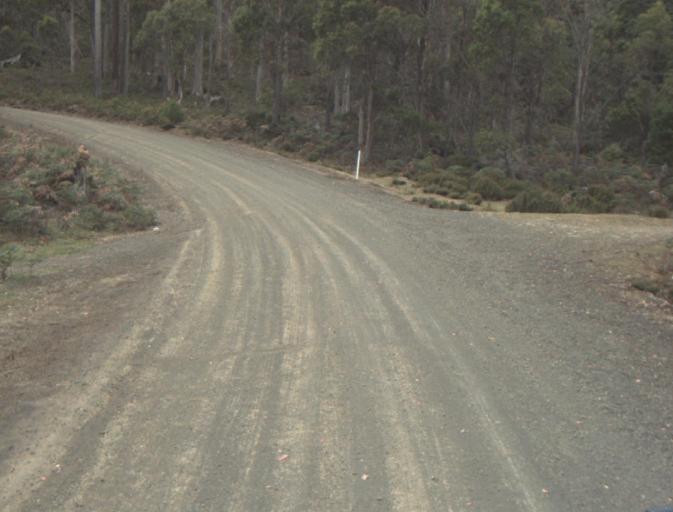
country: AU
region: Tasmania
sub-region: Dorset
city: Scottsdale
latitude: -41.4976
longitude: 147.6000
